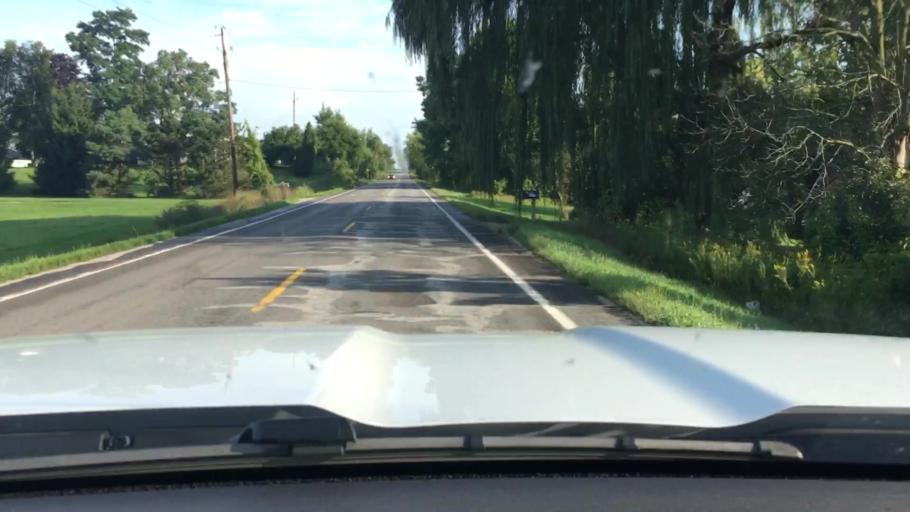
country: US
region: Michigan
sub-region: Kent County
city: Kent City
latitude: 43.2079
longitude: -85.7709
